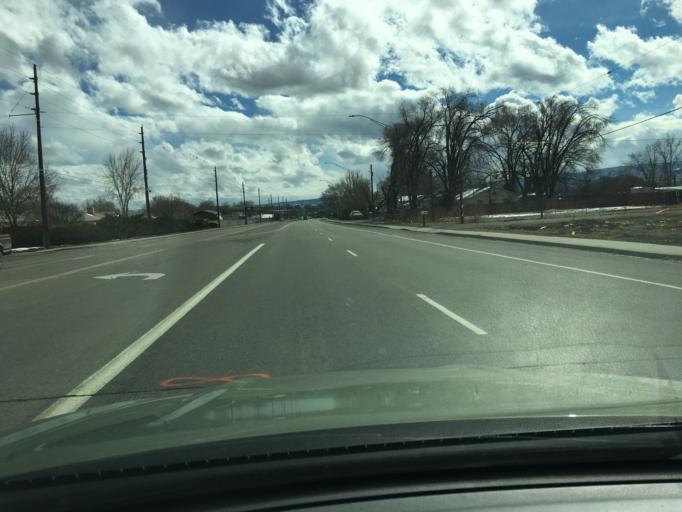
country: US
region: Colorado
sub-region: Mesa County
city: Clifton
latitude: 39.0741
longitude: -108.4594
